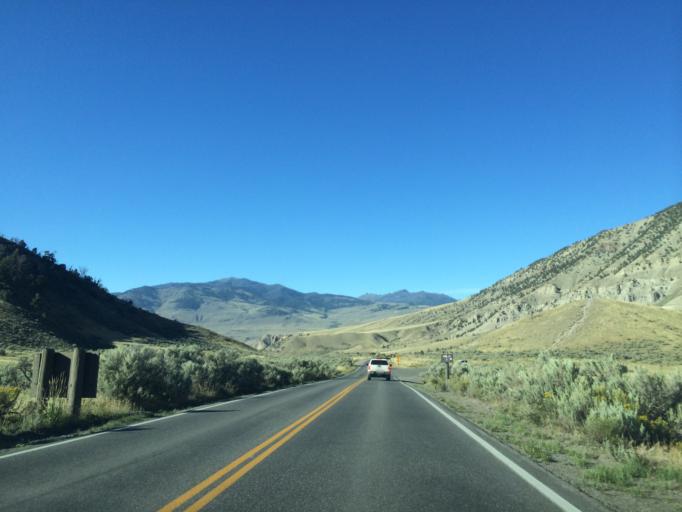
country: US
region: Montana
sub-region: Gallatin County
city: West Yellowstone
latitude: 44.9777
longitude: -110.6926
